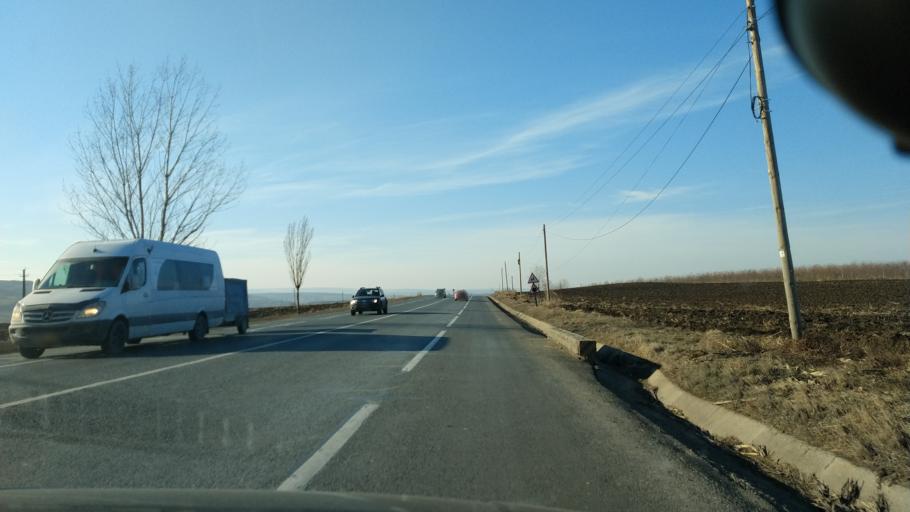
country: RO
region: Iasi
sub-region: Comuna Baltati
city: Baltati
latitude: 47.2189
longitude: 27.1114
